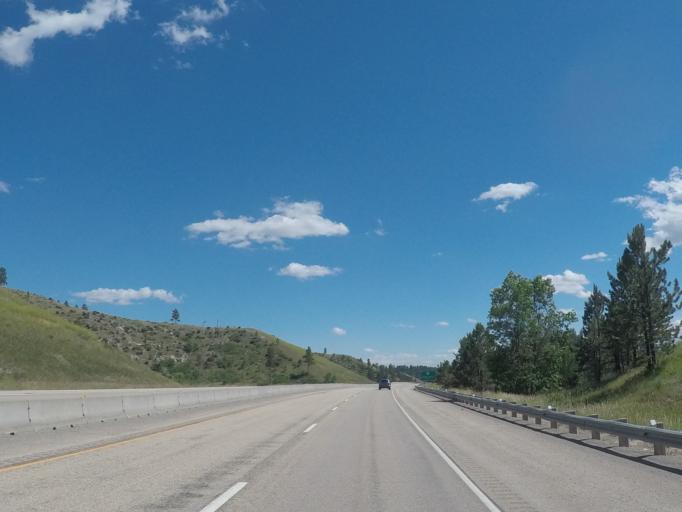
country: US
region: Montana
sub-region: Big Horn County
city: Crow Agency
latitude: 45.3358
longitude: -107.3494
